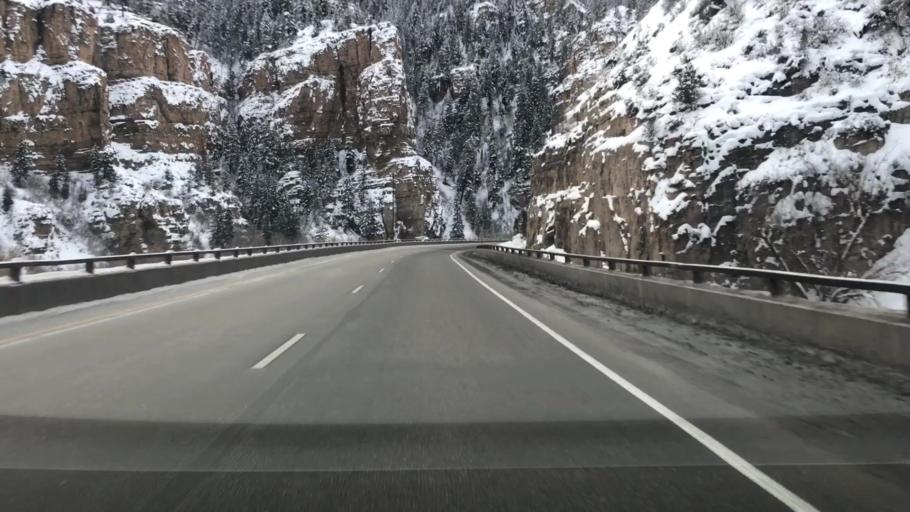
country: US
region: Colorado
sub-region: Garfield County
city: Glenwood Springs
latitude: 39.6064
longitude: -107.1560
